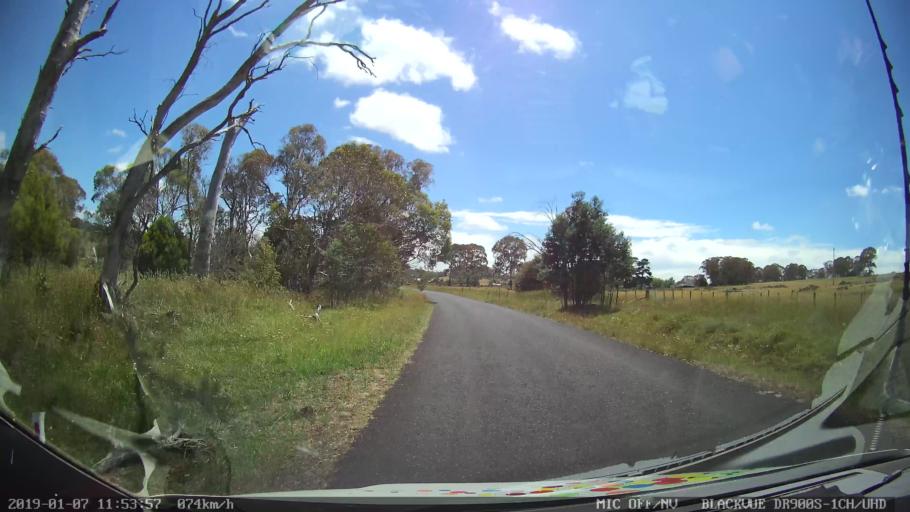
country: AU
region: New South Wales
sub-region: Guyra
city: Guyra
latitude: -30.3011
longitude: 151.6627
